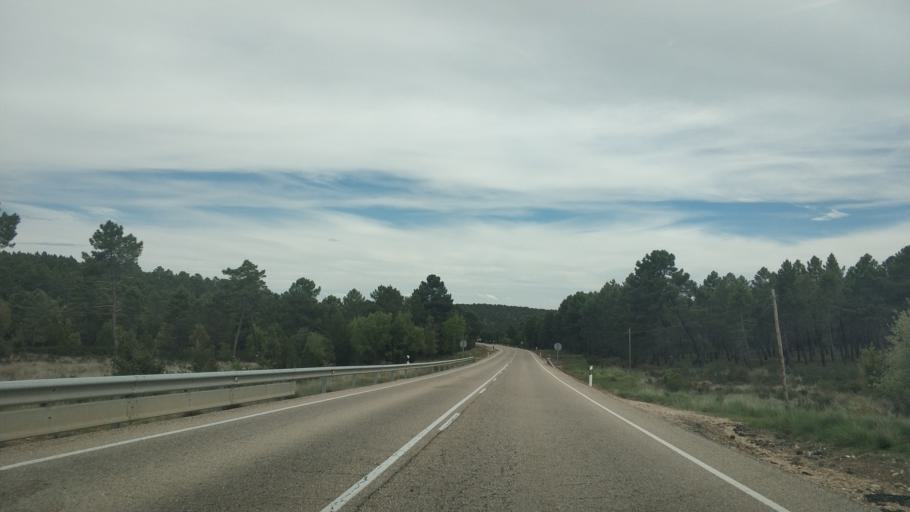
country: ES
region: Castille and Leon
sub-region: Provincia de Soria
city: Bayubas de Abajo
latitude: 41.5182
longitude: -2.9298
